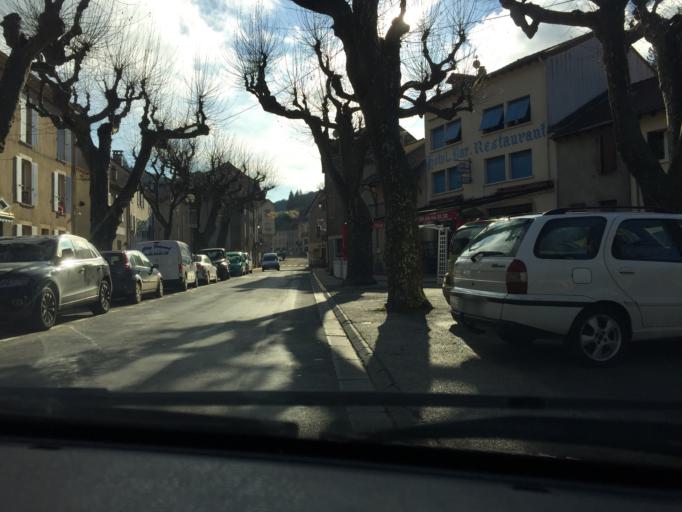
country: FR
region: Rhone-Alpes
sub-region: Departement de l'Ardeche
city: Les Vans
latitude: 44.4398
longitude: 3.9320
